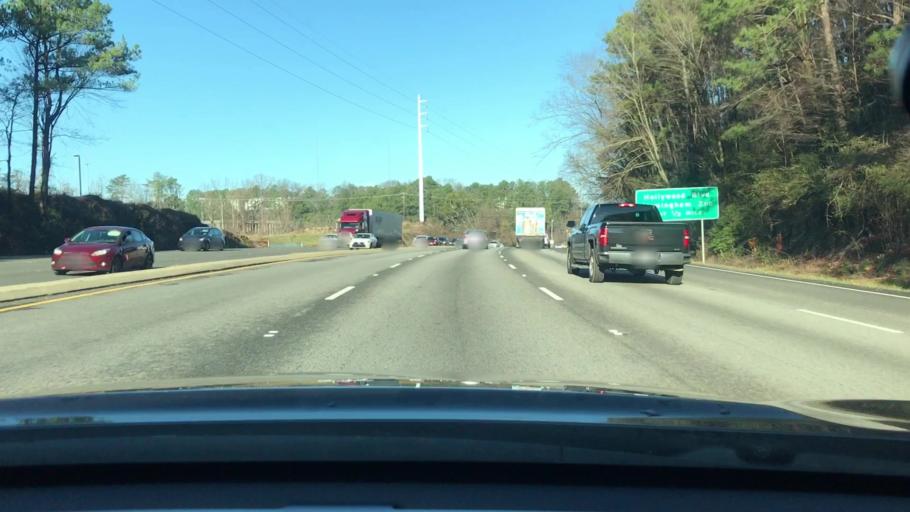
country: US
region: Alabama
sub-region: Jefferson County
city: Homewood
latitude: 33.4760
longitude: -86.7709
